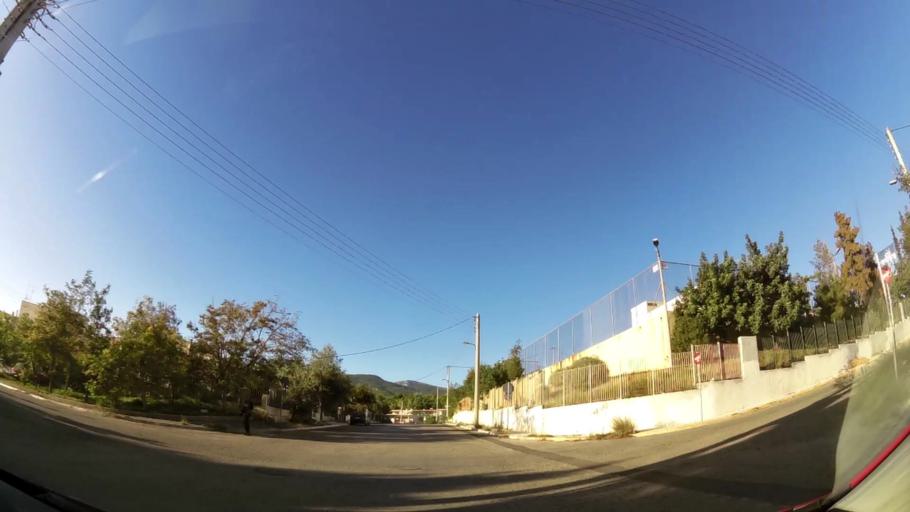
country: GR
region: Attica
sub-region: Nomarchia Anatolikis Attikis
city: Acharnes
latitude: 38.0854
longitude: 23.7208
